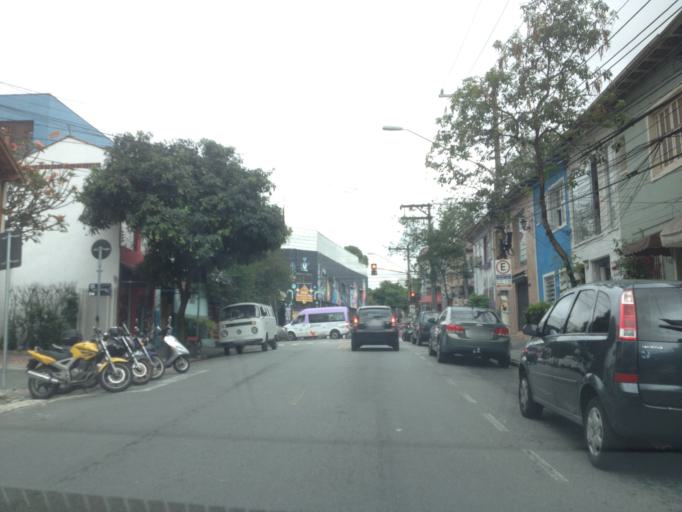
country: BR
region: Sao Paulo
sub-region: Sao Paulo
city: Sao Paulo
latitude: -23.5612
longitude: -46.6865
